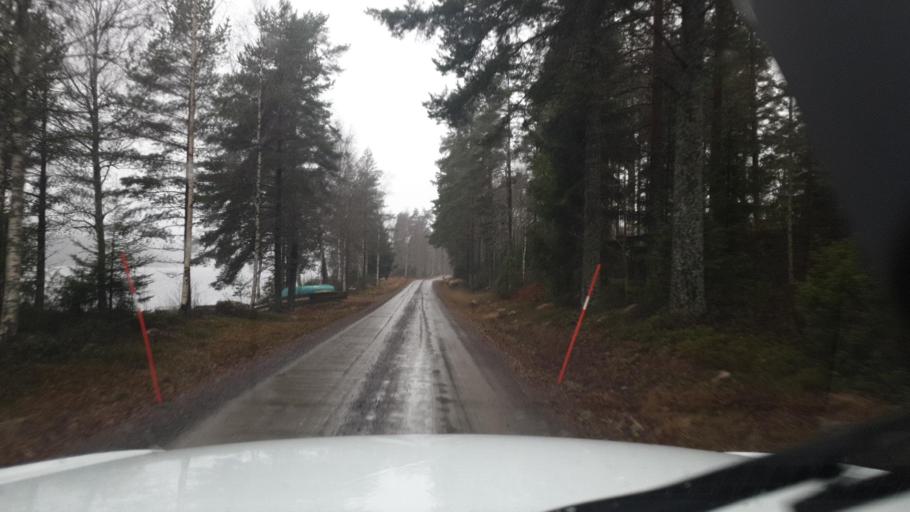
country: SE
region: Vaermland
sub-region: Arvika Kommun
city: Arvika
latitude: 59.8681
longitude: 12.8100
